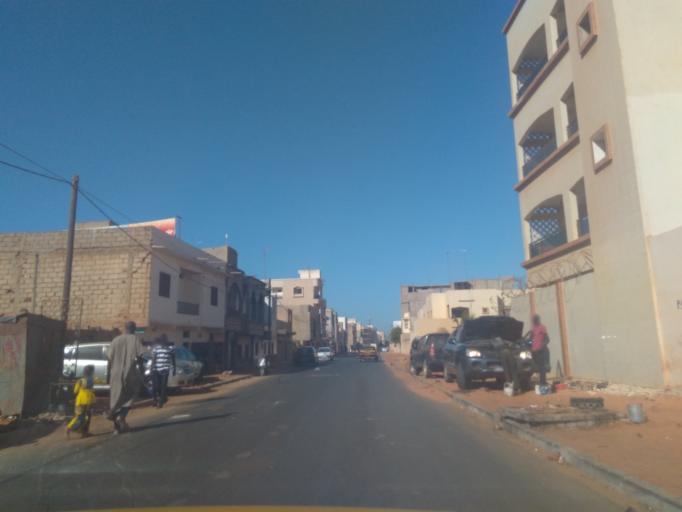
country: SN
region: Dakar
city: Pikine
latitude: 14.7723
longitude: -17.4149
